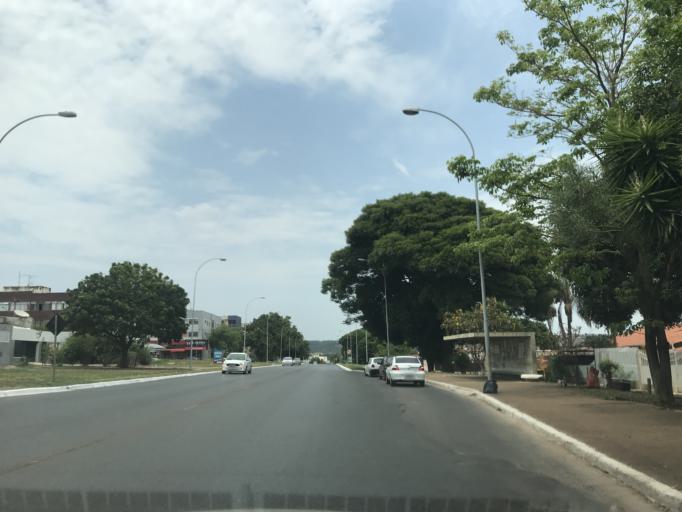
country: BR
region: Federal District
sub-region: Brasilia
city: Brasilia
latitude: -15.6578
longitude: -47.8054
